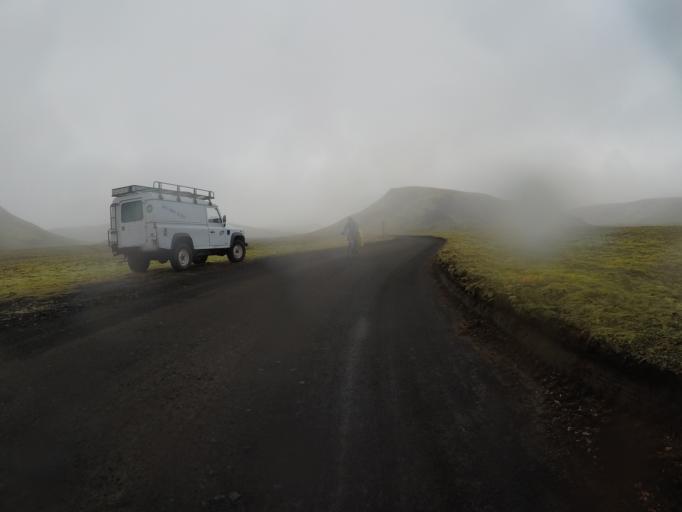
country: IS
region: South
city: Vestmannaeyjar
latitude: 63.9682
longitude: -18.8199
